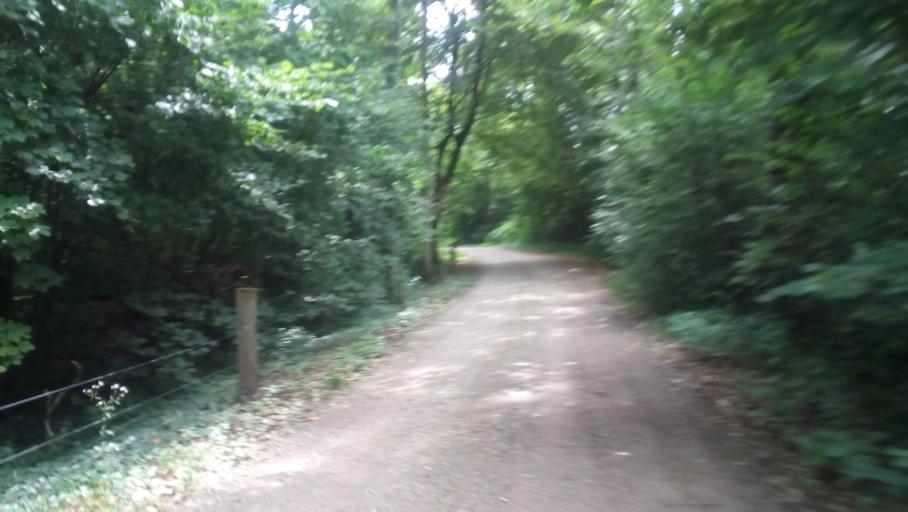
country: DE
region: Baden-Wuerttemberg
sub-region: Freiburg Region
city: Rheinau
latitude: 48.6936
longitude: 7.9546
